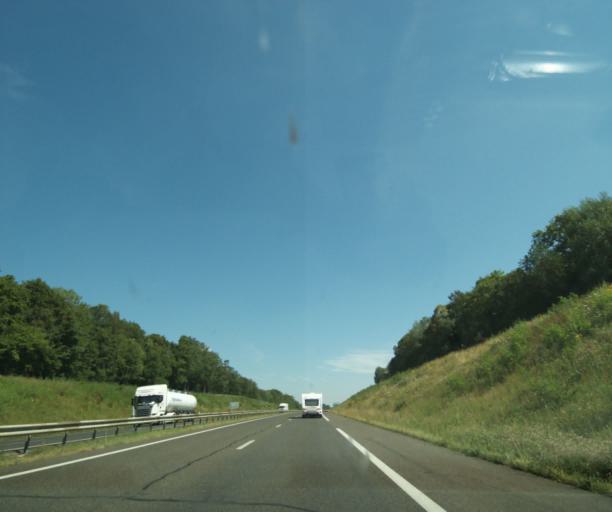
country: FR
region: Lorraine
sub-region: Departement de Meurthe-et-Moselle
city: Dommartin-les-Toul
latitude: 48.6376
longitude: 5.8809
